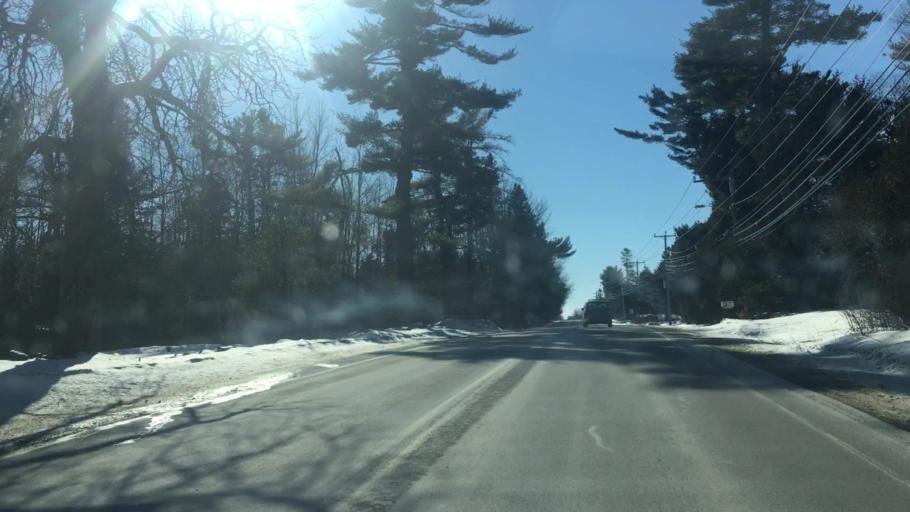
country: US
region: Maine
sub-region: Hancock County
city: Ellsworth
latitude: 44.5193
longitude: -68.4313
